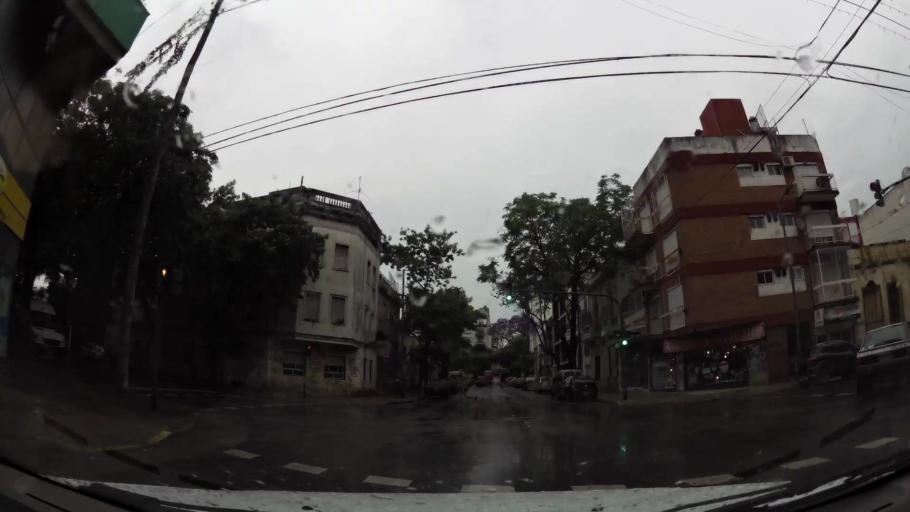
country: AR
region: Buenos Aires F.D.
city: Colegiales
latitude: -34.5929
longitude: -58.4303
